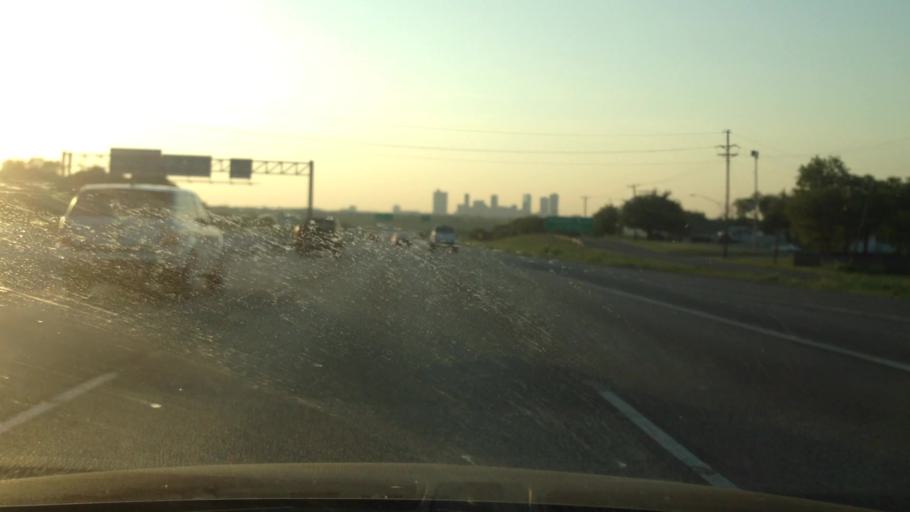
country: US
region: Texas
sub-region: Tarrant County
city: Fort Worth
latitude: 32.7157
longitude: -97.2827
